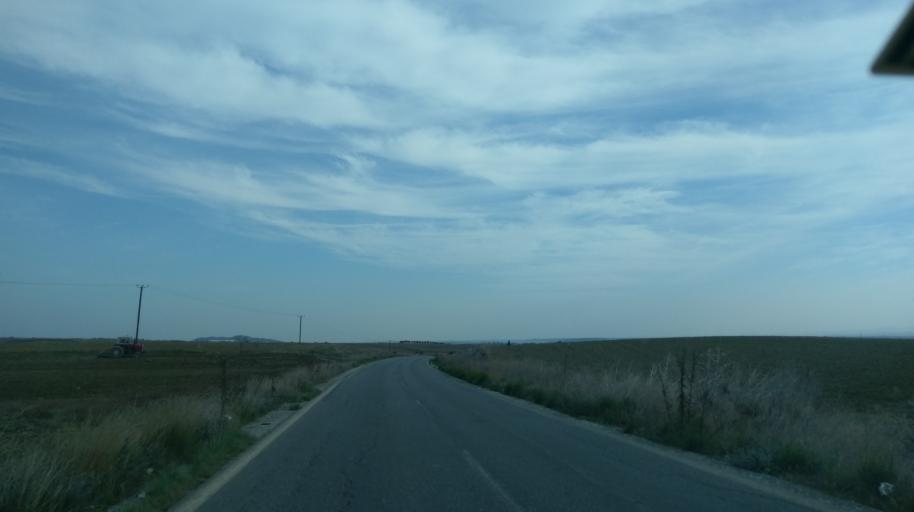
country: CY
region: Keryneia
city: Lapithos
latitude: 35.2503
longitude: 33.1491
